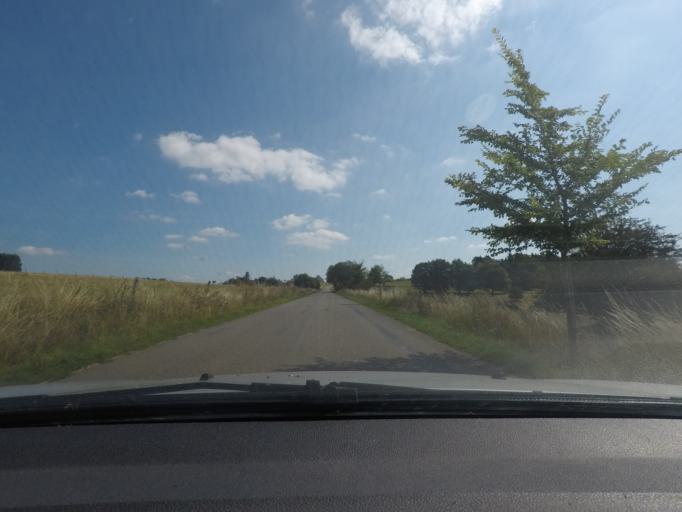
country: BE
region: Wallonia
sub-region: Province du Luxembourg
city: Habay-la-Vieille
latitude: 49.7870
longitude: 5.6143
